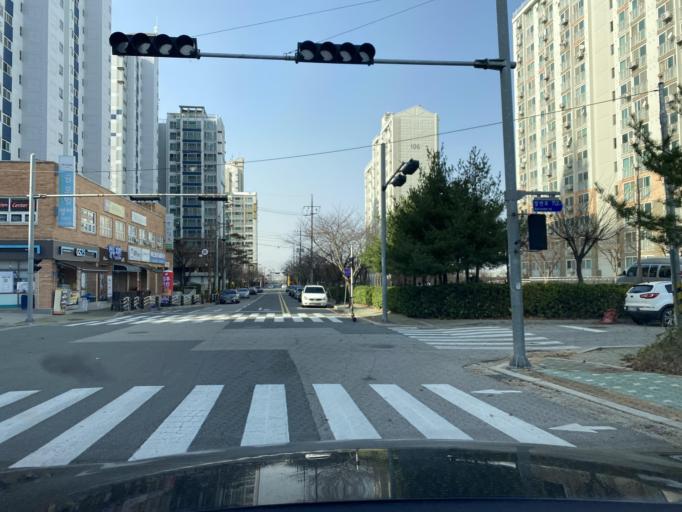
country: KR
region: Chungcheongnam-do
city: Yesan
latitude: 36.6962
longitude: 126.8354
